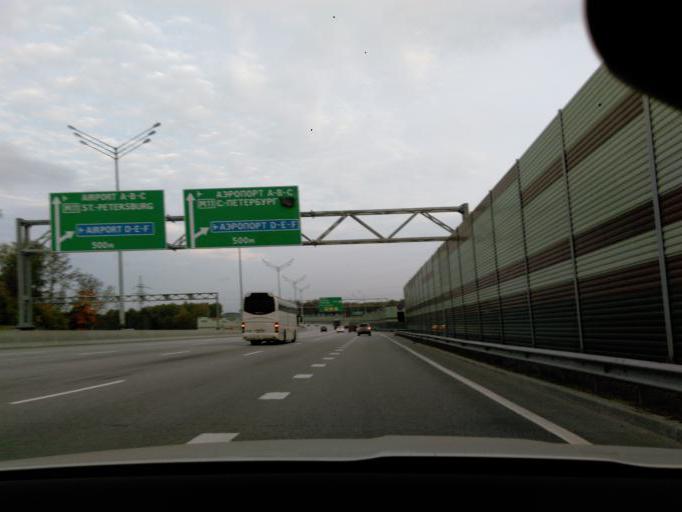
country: RU
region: Moscow
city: Khimki
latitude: 55.9522
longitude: 37.4335
